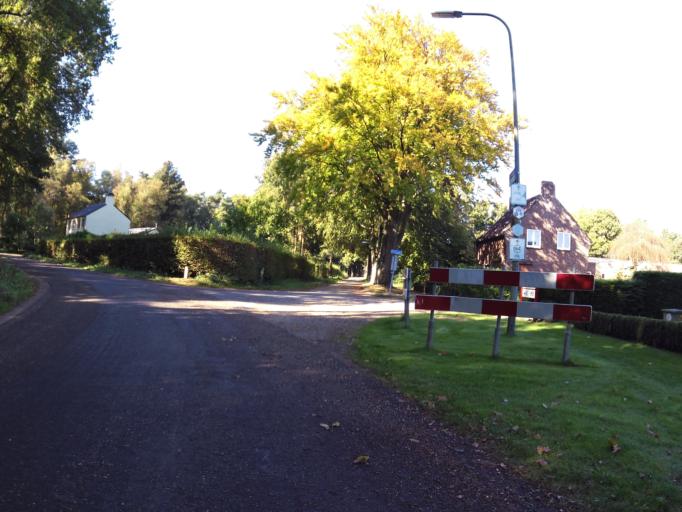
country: NL
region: Limburg
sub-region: Gemeente Venlo
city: Arcen
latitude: 51.4545
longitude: 6.1996
